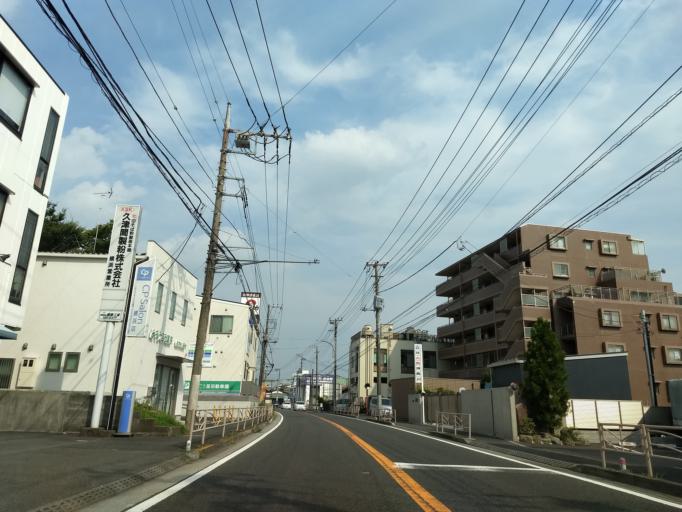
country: JP
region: Kanagawa
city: Minami-rinkan
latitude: 35.4855
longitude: 139.5222
